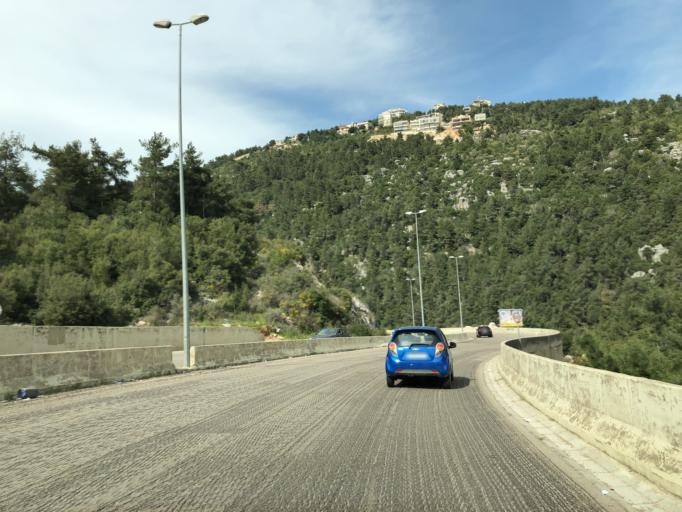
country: LB
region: Mont-Liban
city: Bhamdoun el Mhatta
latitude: 33.8930
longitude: 35.6572
